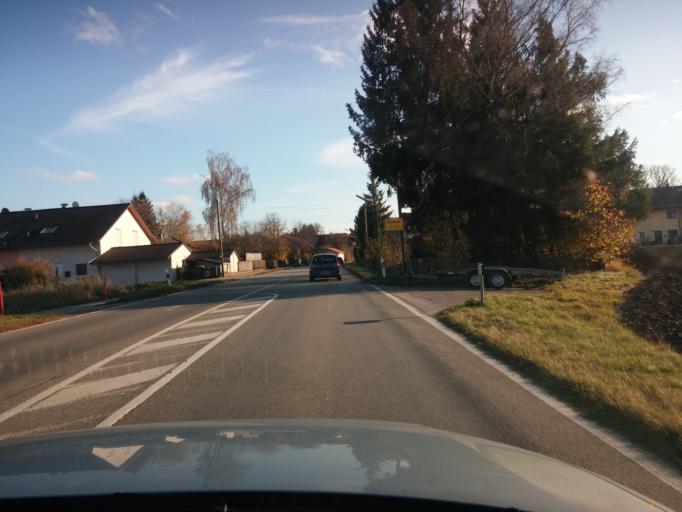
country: DE
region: Bavaria
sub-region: Upper Bavaria
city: Hohenkirchen-Siegertsbrunn
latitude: 47.9965
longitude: 11.7333
